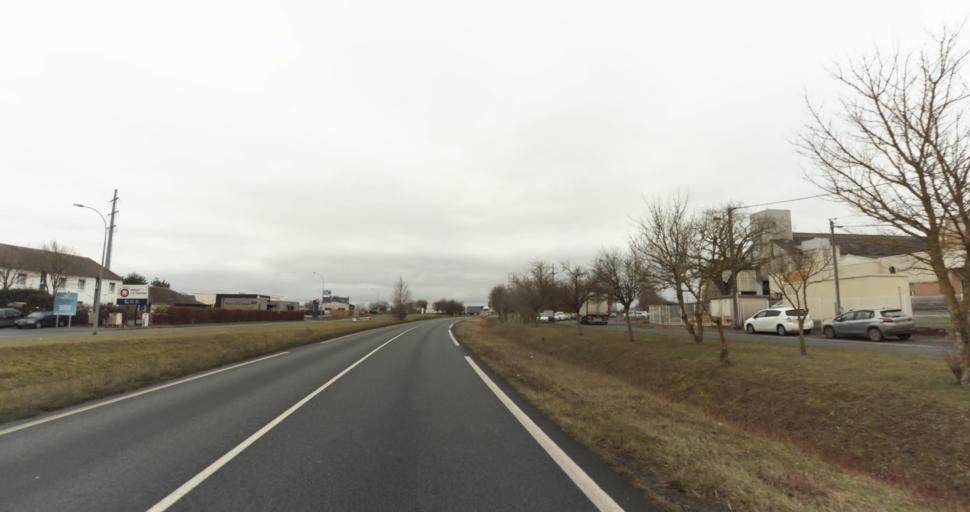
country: FR
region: Pays de la Loire
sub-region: Departement de Maine-et-Loire
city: Doue-la-Fontaine
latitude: 47.1844
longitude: -0.2449
